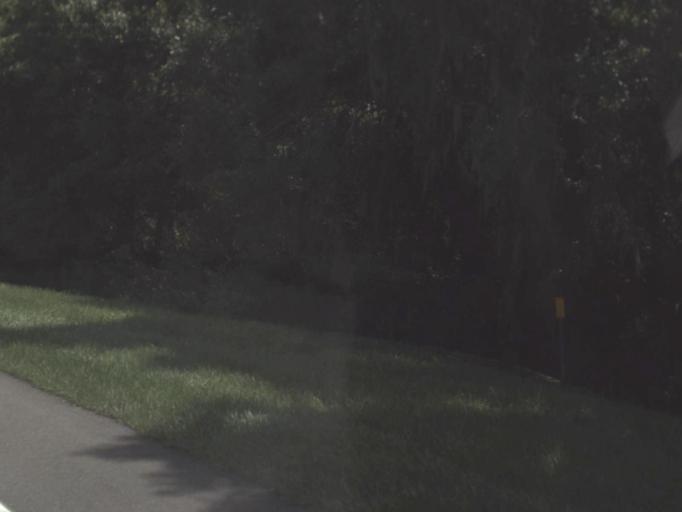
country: US
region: Florida
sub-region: Sarasota County
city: The Meadows
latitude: 27.4163
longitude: -82.3551
